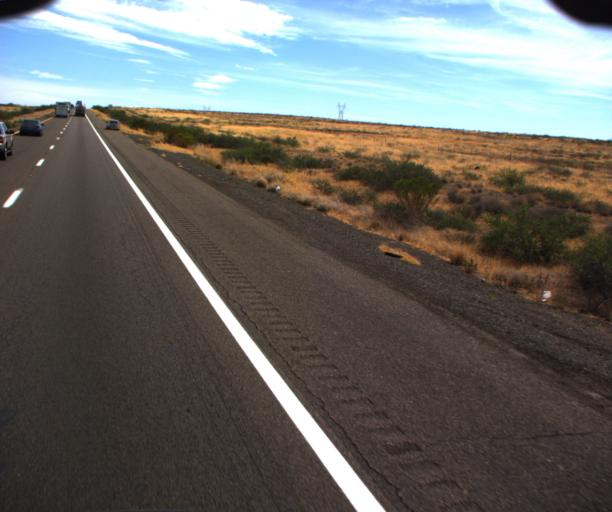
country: US
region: Arizona
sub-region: Yavapai County
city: Cordes Lakes
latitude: 34.2010
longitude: -112.1256
